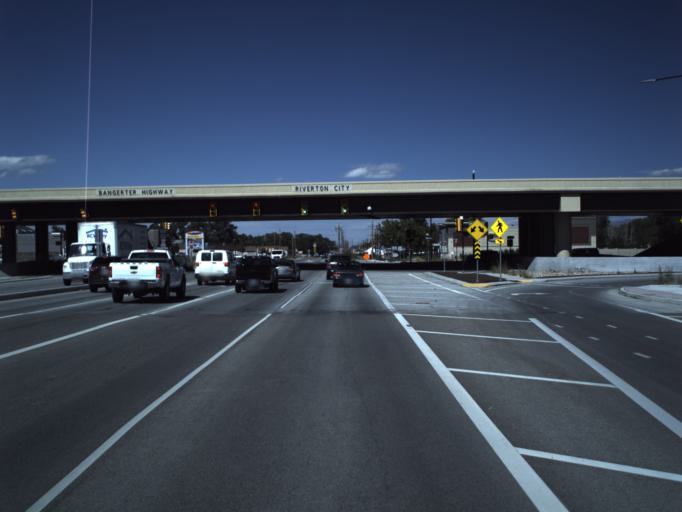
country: US
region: Utah
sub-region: Salt Lake County
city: Bluffdale
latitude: 40.4998
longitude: -111.9386
